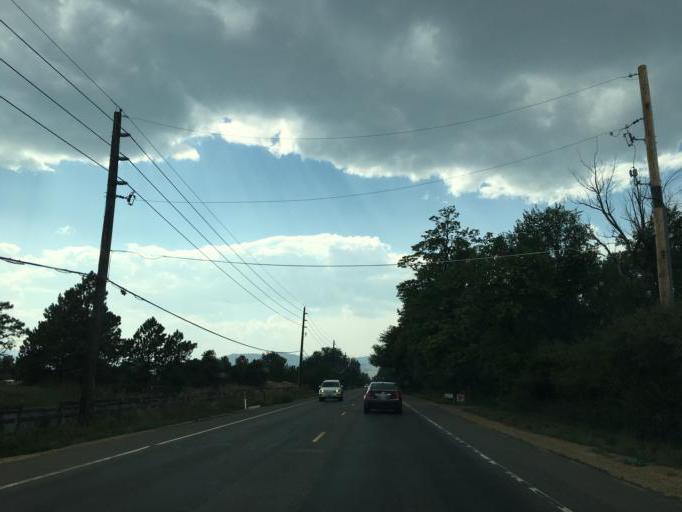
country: US
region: Colorado
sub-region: Boulder County
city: Gunbarrel
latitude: 40.0510
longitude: -105.2111
